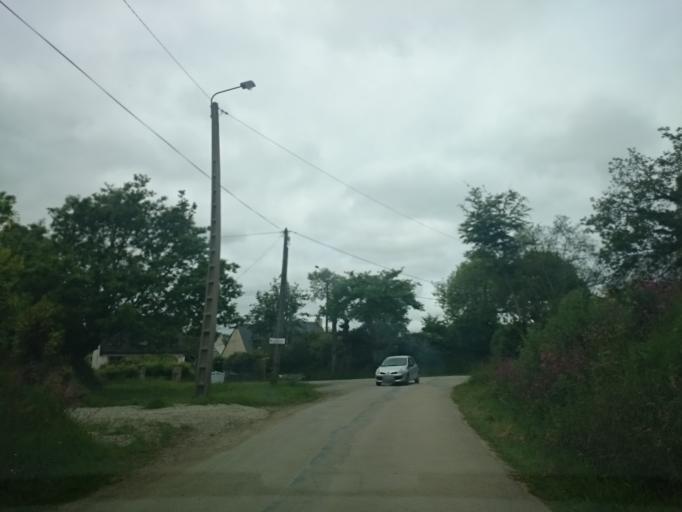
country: FR
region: Brittany
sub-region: Departement du Finistere
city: Gouesnou
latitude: 48.4548
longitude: -4.4526
